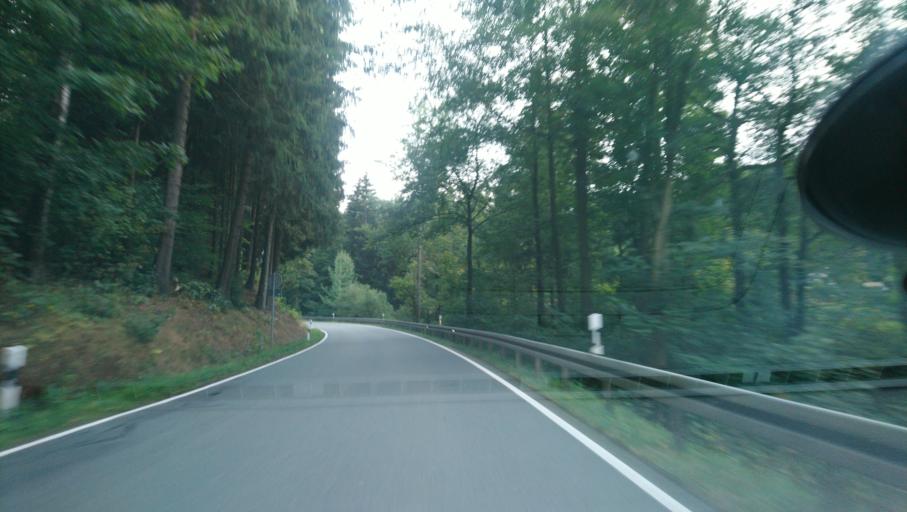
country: DE
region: Saxony
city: Annaberg-Buchholz
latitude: 50.5982
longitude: 12.9957
